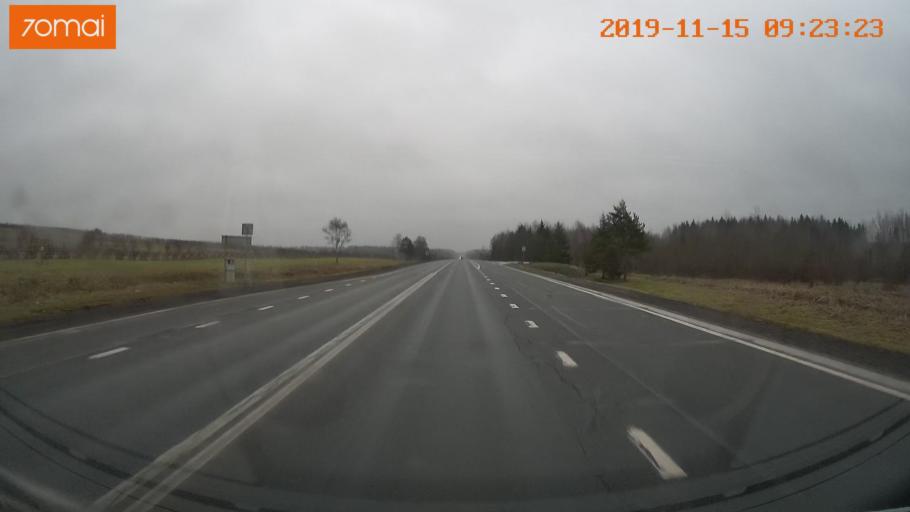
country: RU
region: Vologda
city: Tonshalovo
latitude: 59.3002
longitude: 38.1071
